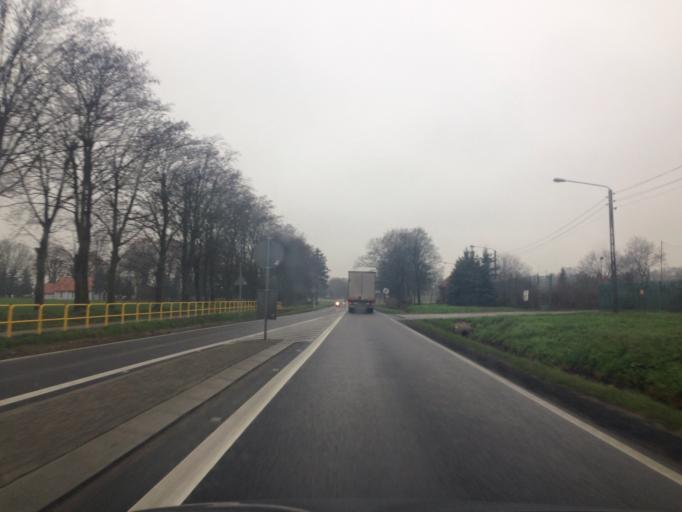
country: PL
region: Kujawsko-Pomorskie
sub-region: Powiat nakielski
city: Naklo nad Notecia
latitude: 53.1586
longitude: 17.6315
